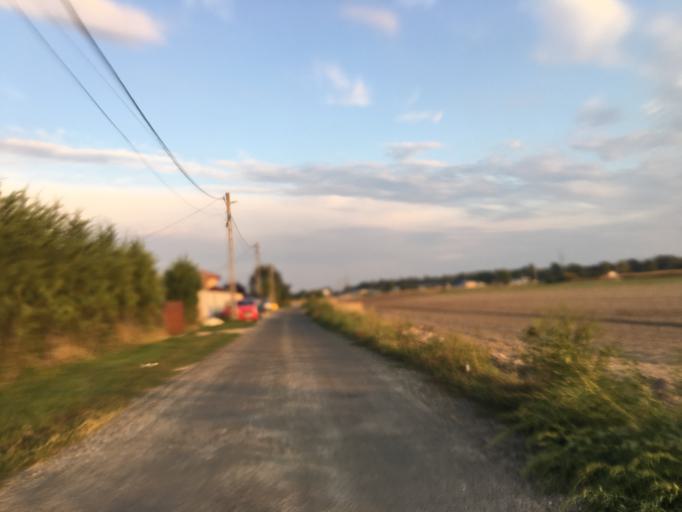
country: HU
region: Pest
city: Szigetszentmiklos
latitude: 47.3435
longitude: 19.0191
